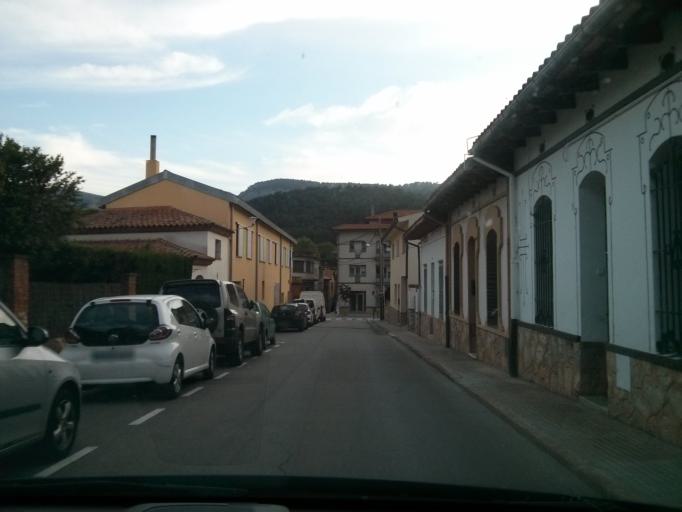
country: ES
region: Catalonia
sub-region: Provincia de Barcelona
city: Aiguafreda
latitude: 41.7682
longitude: 2.2521
